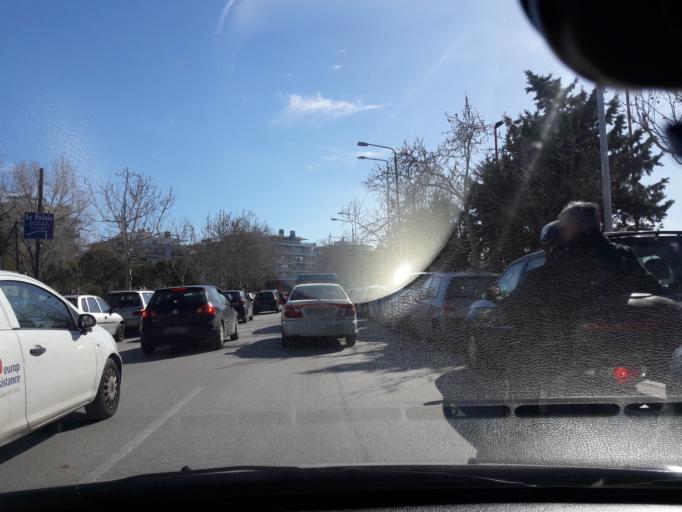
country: GR
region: Central Macedonia
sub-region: Nomos Thessalonikis
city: Kalamaria
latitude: 40.5961
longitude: 22.9503
